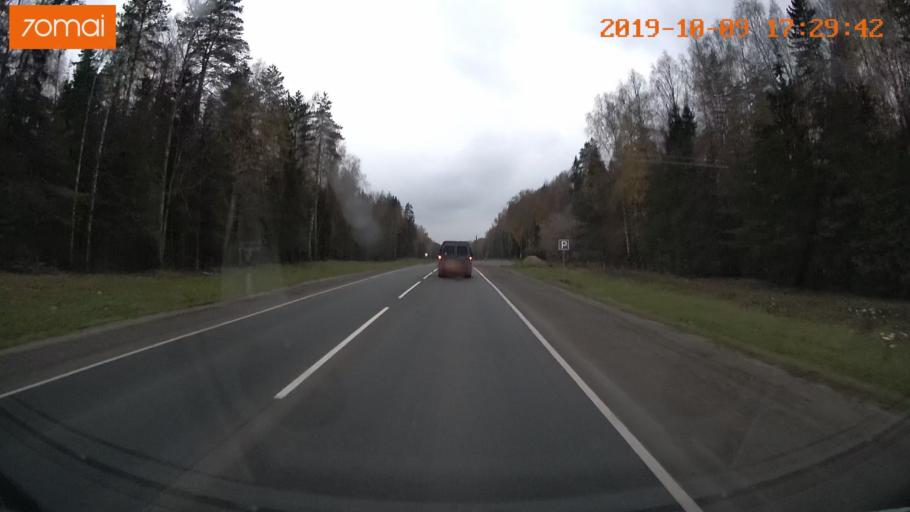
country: RU
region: Ivanovo
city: Bogorodskoye
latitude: 57.1482
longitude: 41.0570
